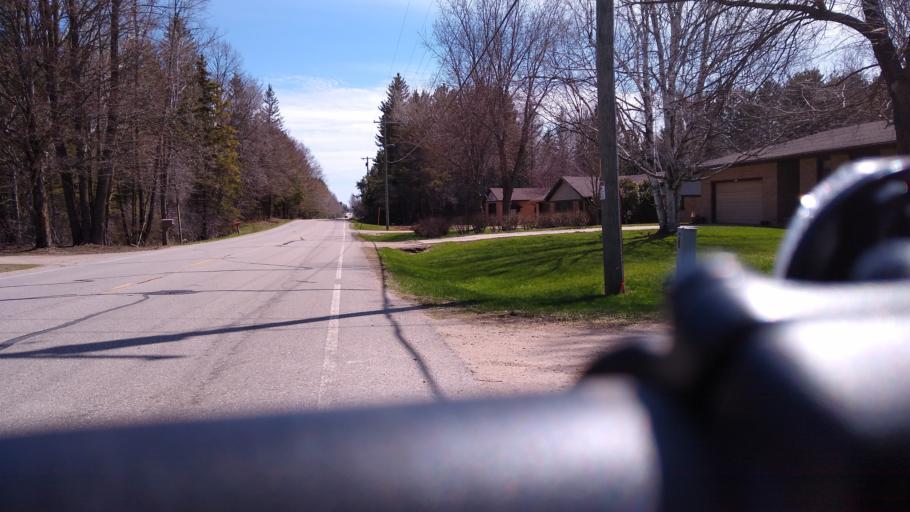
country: US
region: Michigan
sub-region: Delta County
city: Escanaba
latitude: 45.7316
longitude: -87.2025
